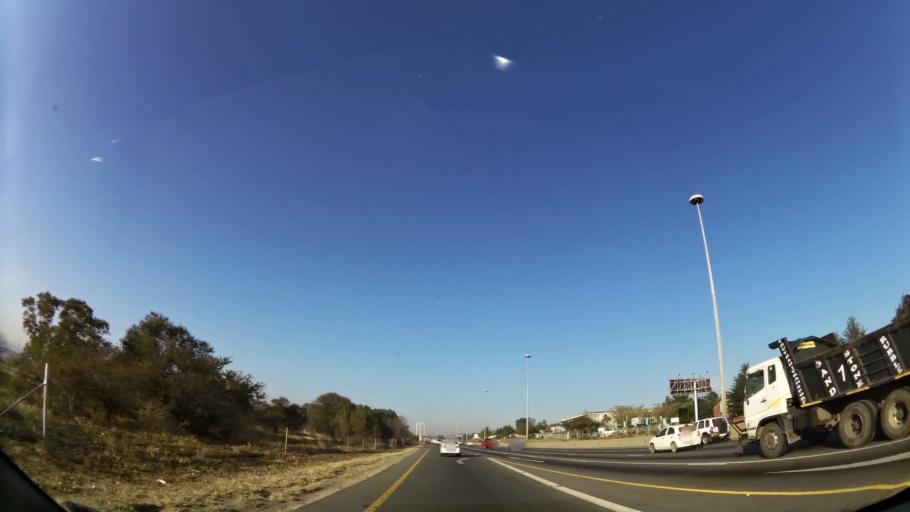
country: ZA
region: Gauteng
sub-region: City of Johannesburg Metropolitan Municipality
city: Johannesburg
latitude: -26.2026
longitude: 28.0240
